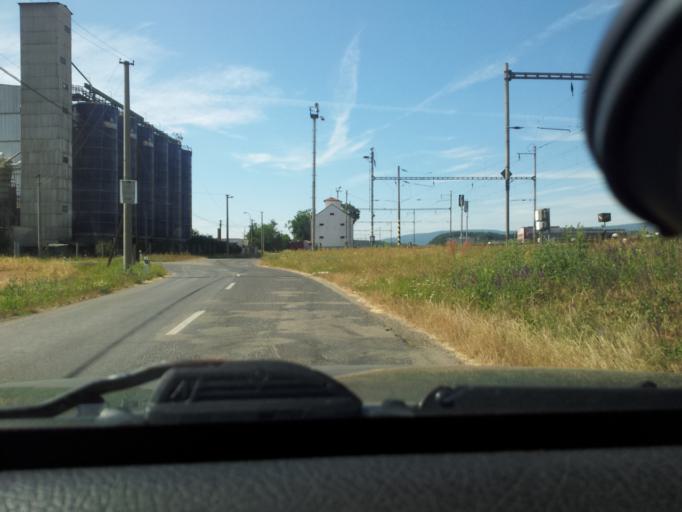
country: SK
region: Nitriansky
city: Tlmace
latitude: 48.2787
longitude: 18.5509
